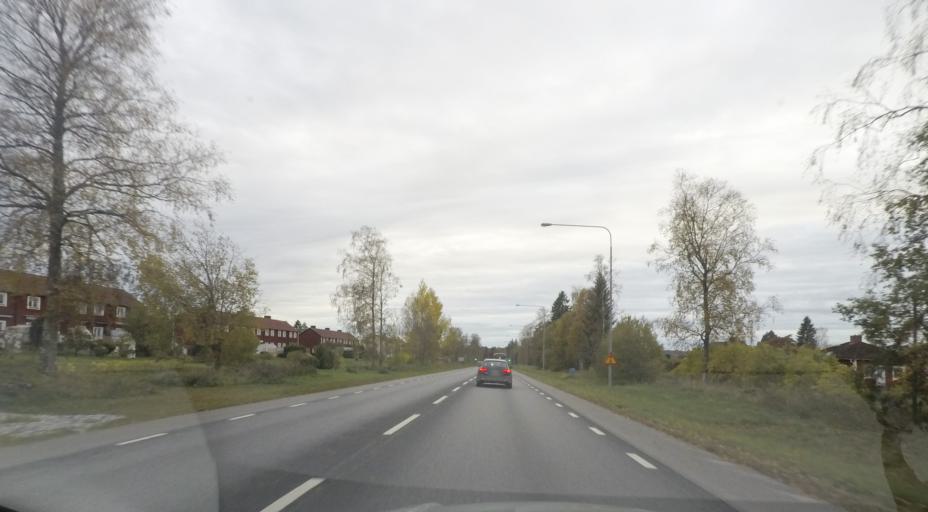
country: SE
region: OErebro
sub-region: Hallefors Kommun
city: Haellefors
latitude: 59.7801
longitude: 14.5294
